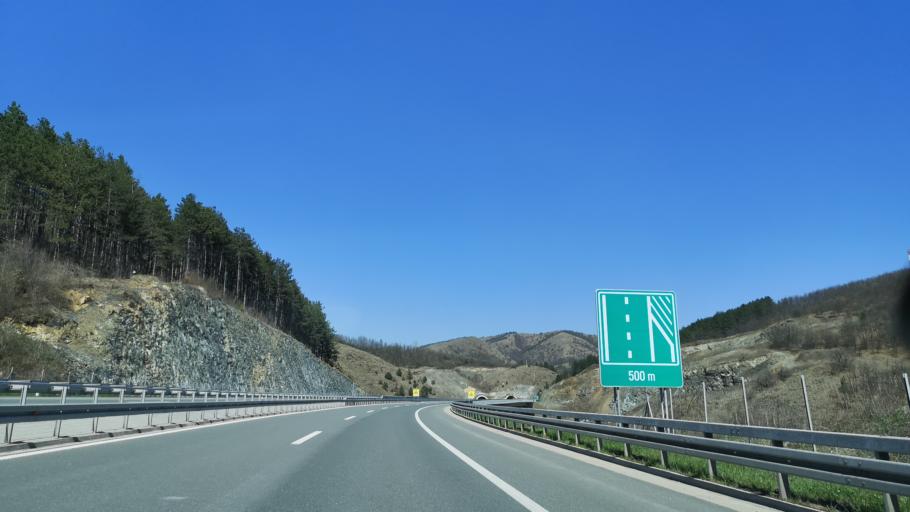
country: RS
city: Prislonica
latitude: 43.9722
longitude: 20.3963
